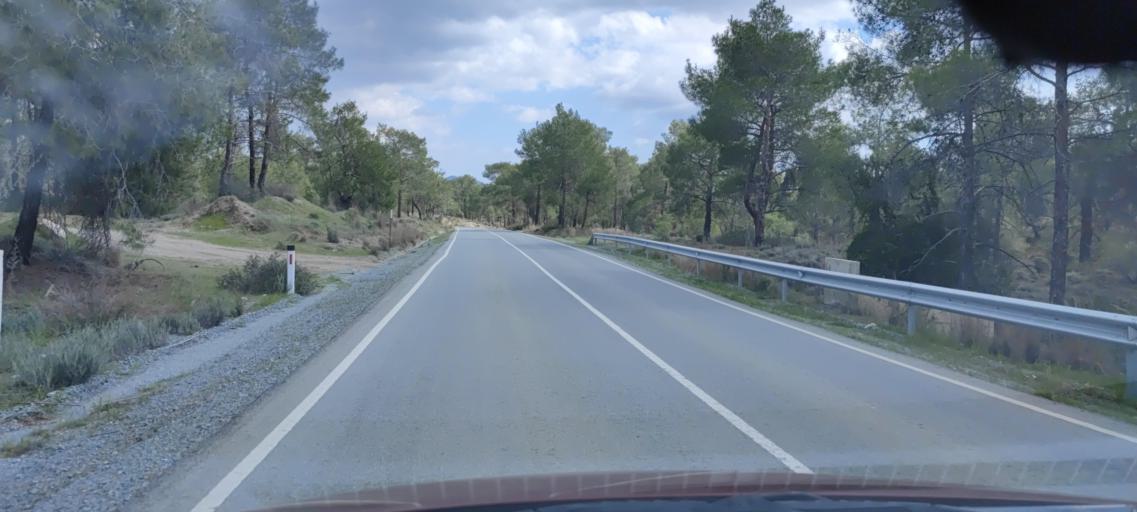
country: CY
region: Lefkosia
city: Lythrodontas
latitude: 34.9277
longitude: 33.3433
